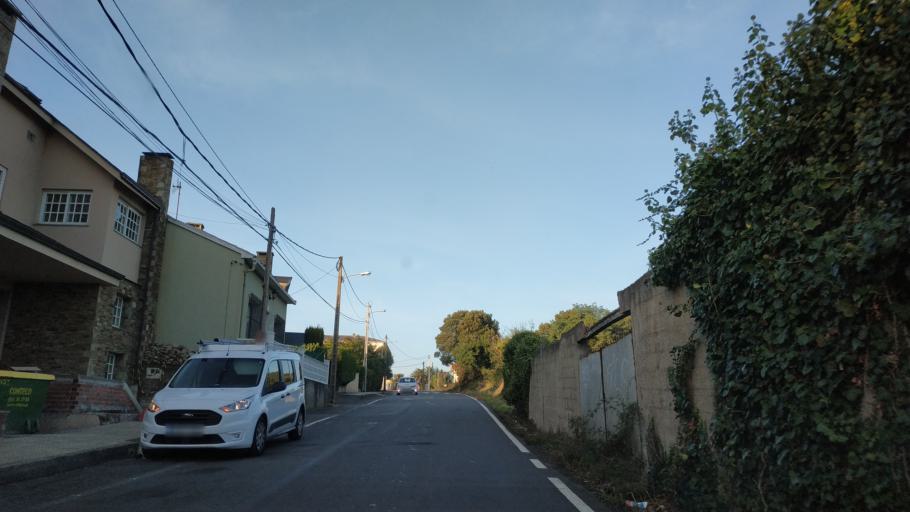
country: ES
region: Galicia
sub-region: Provincia da Coruna
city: Oleiros
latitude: 43.3524
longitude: -8.3455
